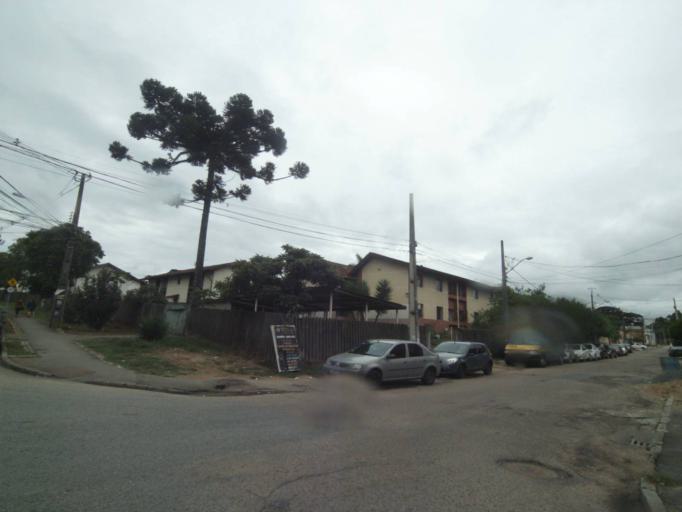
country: BR
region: Parana
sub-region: Curitiba
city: Curitiba
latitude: -25.4600
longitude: -49.3400
